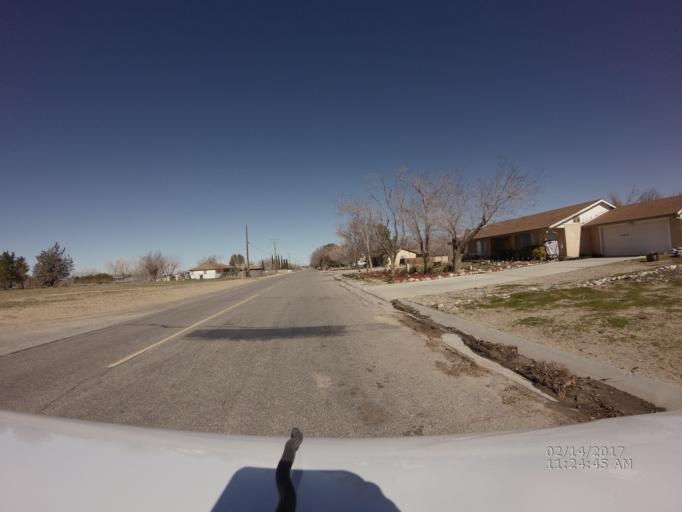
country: US
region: California
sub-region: Los Angeles County
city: Littlerock
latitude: 34.5616
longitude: -117.9608
